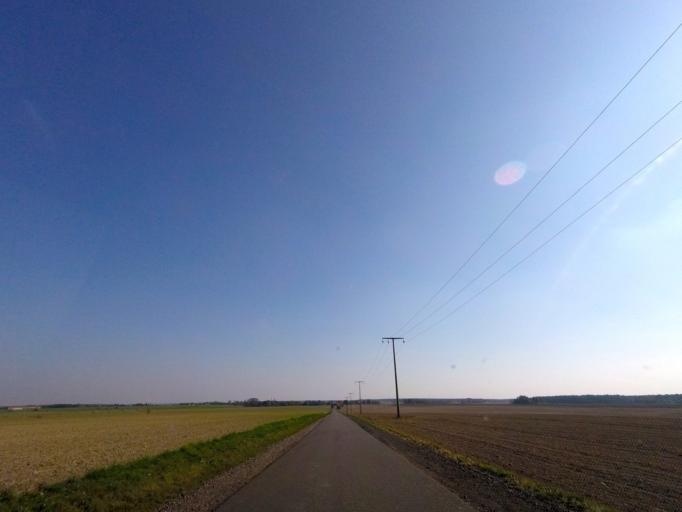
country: DE
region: Brandenburg
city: Niedergorsdorf
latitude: 51.9385
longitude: 13.0172
